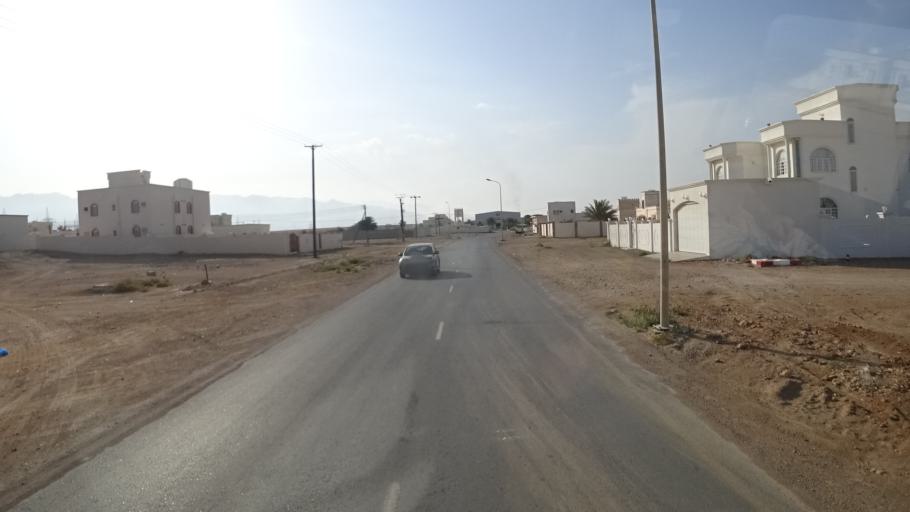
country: OM
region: Ash Sharqiyah
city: Sur
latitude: 22.6193
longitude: 59.4576
